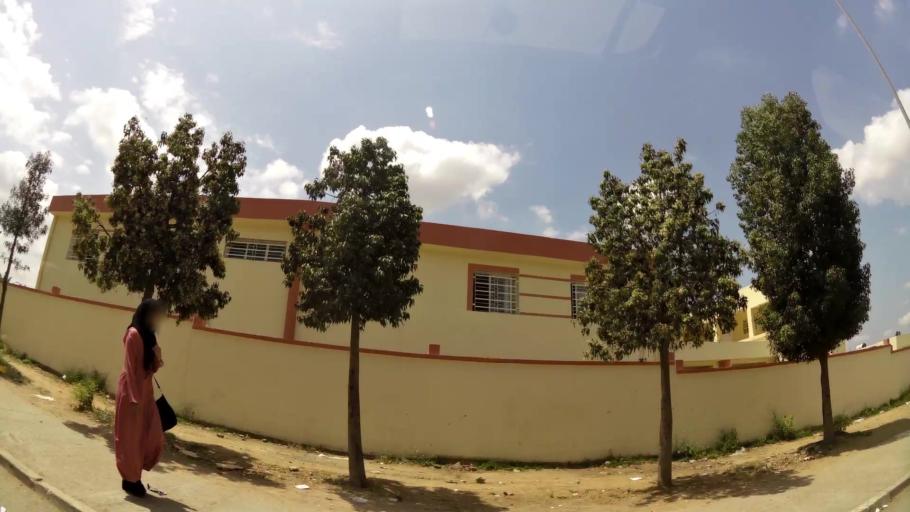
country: MA
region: Rabat-Sale-Zemmour-Zaer
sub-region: Khemisset
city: Tiflet
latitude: 34.0068
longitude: -6.5307
